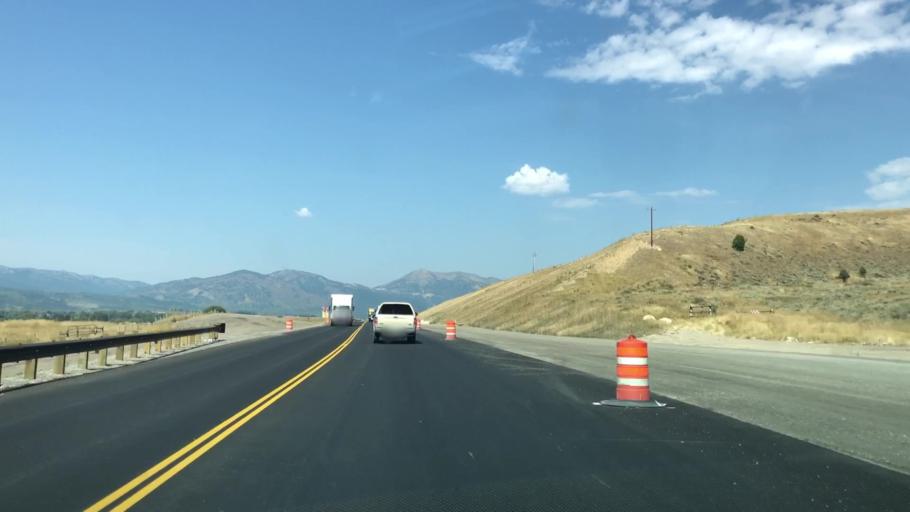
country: US
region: Wyoming
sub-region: Teton County
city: South Park
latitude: 43.4059
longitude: -110.7606
